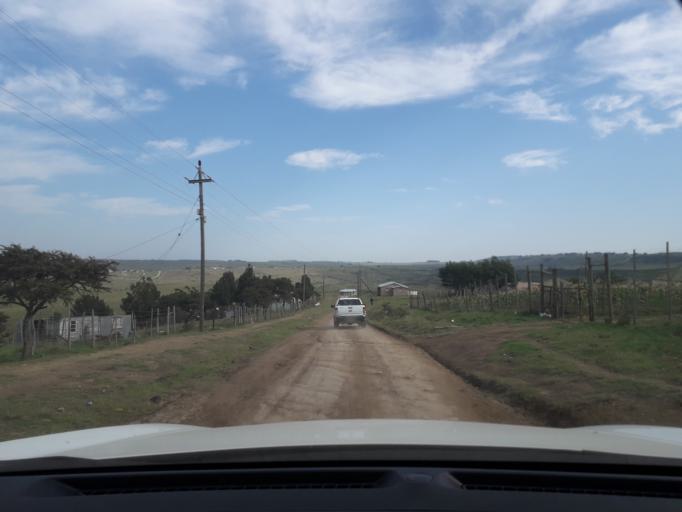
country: ZA
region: Eastern Cape
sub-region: Buffalo City Metropolitan Municipality
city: Bhisho
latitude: -32.9923
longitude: 27.3537
